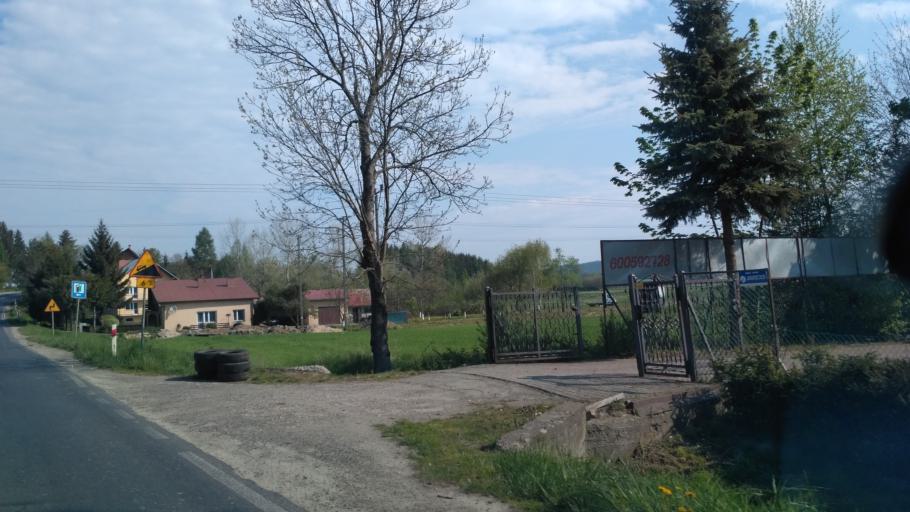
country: PL
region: Subcarpathian Voivodeship
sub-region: Powiat rzeszowski
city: Dynow
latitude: 49.8244
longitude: 22.2340
